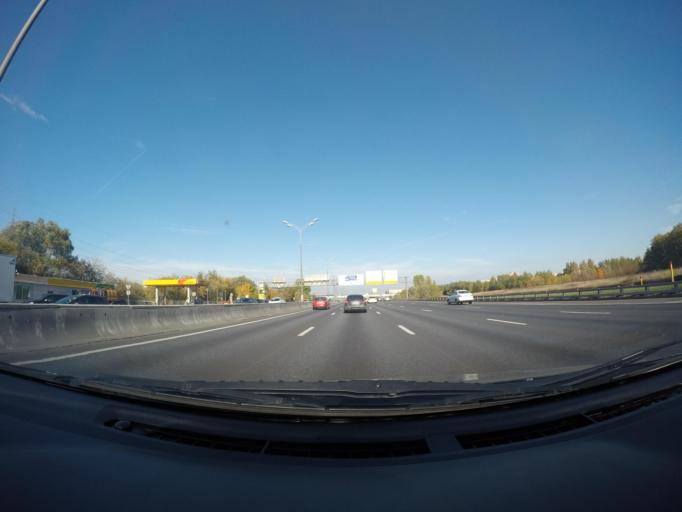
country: RU
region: Moskovskaya
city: Kuskovo
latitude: 55.7248
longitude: 37.8398
